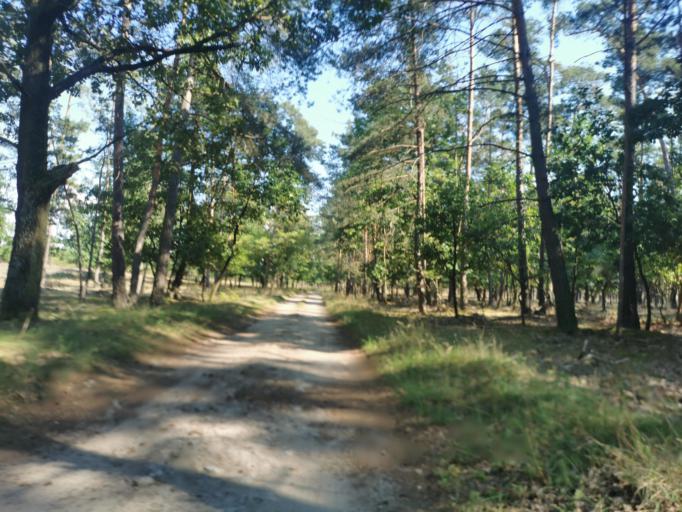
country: SK
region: Trnavsky
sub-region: Okres Senica
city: Senica
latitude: 48.6433
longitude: 17.2731
